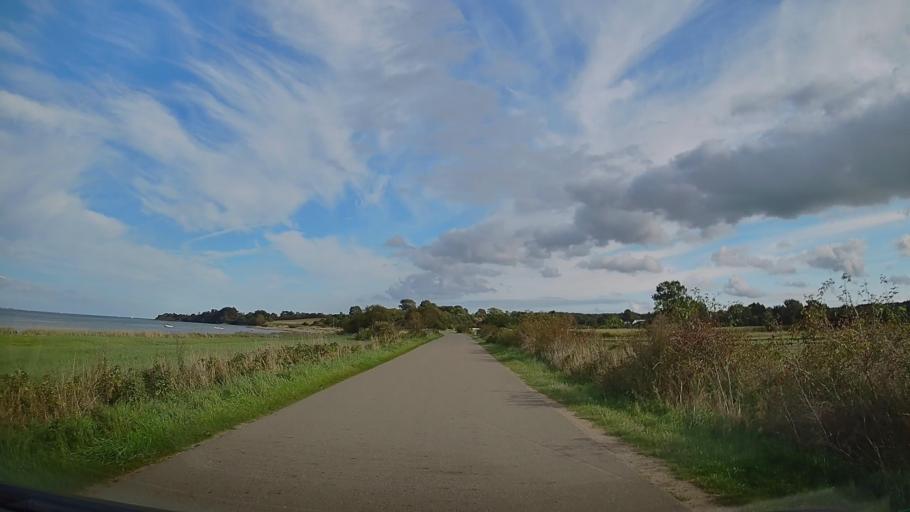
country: DE
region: Schleswig-Holstein
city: Steinberg
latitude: 54.7959
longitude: 9.7699
